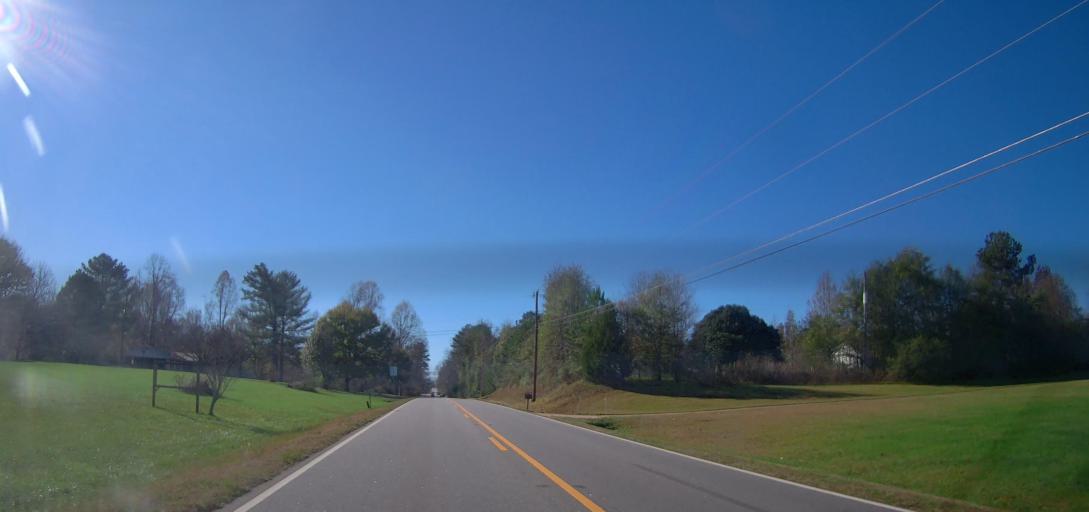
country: US
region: Georgia
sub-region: White County
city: Cleveland
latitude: 34.4774
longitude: -83.7623
